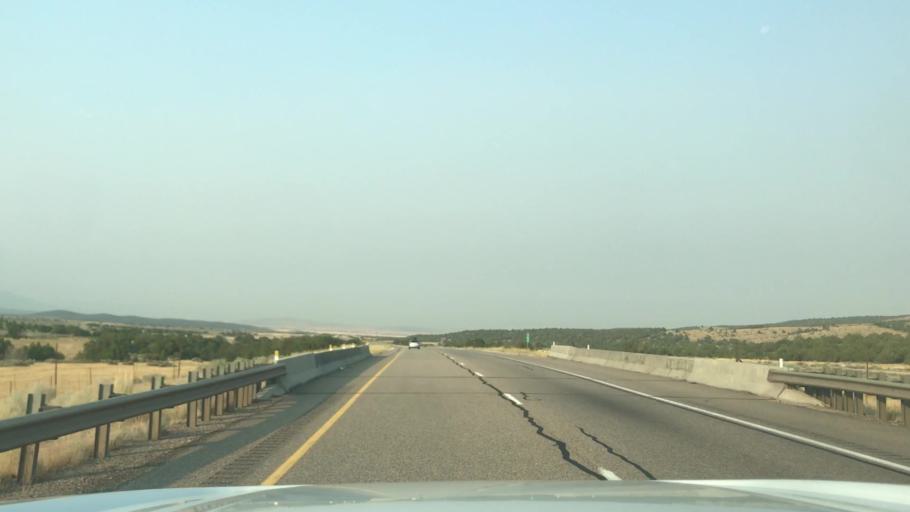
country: US
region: Utah
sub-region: Millard County
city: Fillmore
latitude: 39.1892
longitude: -112.1965
